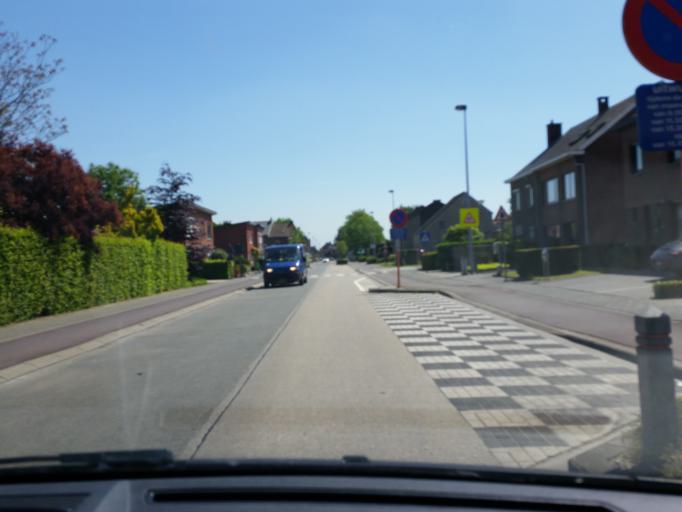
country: BE
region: Flanders
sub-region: Provincie Antwerpen
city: Mechelen
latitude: 51.0444
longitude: 4.5056
